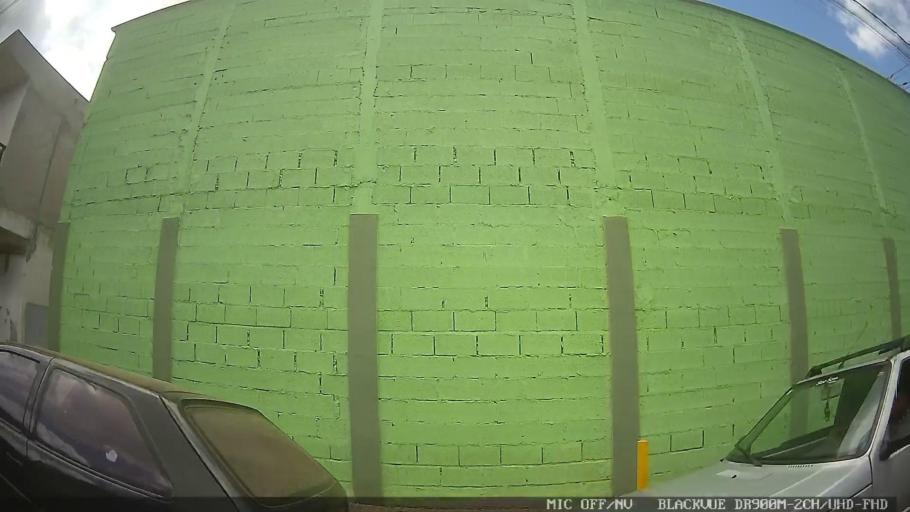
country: BR
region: Minas Gerais
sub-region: Extrema
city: Extrema
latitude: -22.8658
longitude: -46.3358
